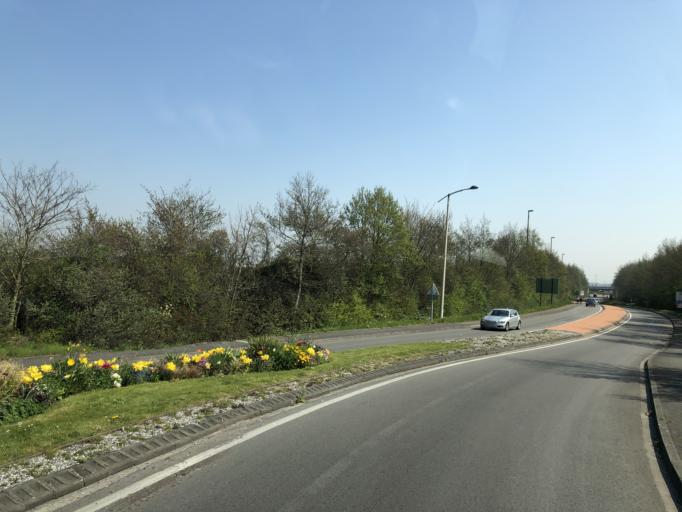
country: FR
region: Nord-Pas-de-Calais
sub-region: Departement du Pas-de-Calais
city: Coquelles
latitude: 50.9291
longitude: 1.7983
